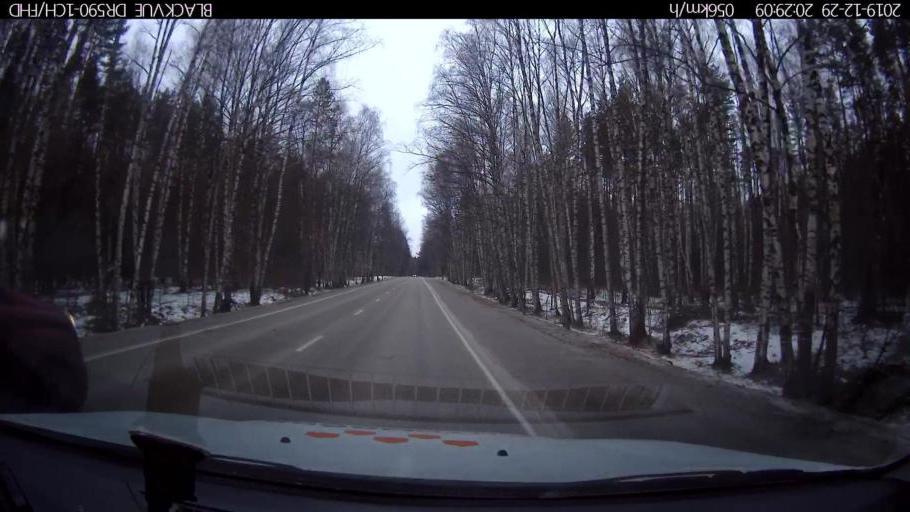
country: RU
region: Nizjnij Novgorod
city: Afonino
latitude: 56.1826
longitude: 44.1064
